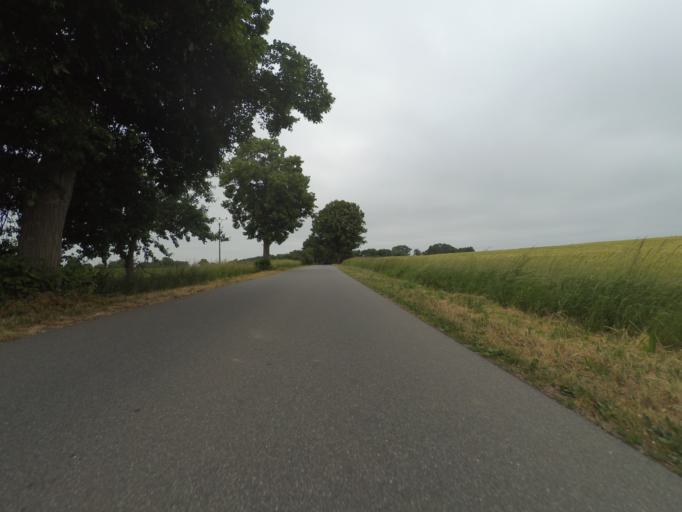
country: DE
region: Mecklenburg-Vorpommern
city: Goldberg
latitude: 53.5347
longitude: 12.1549
